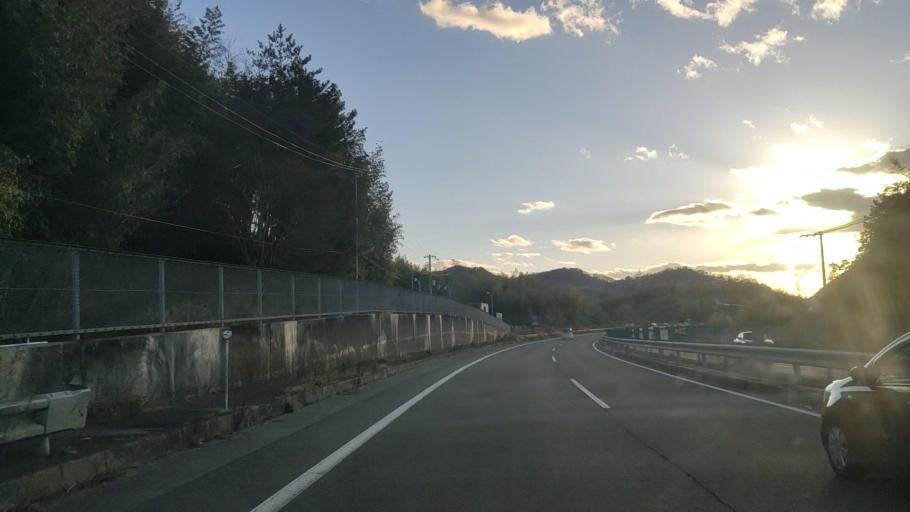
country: JP
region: Hyogo
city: Tatsunocho-tominaga
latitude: 34.8618
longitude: 134.6178
